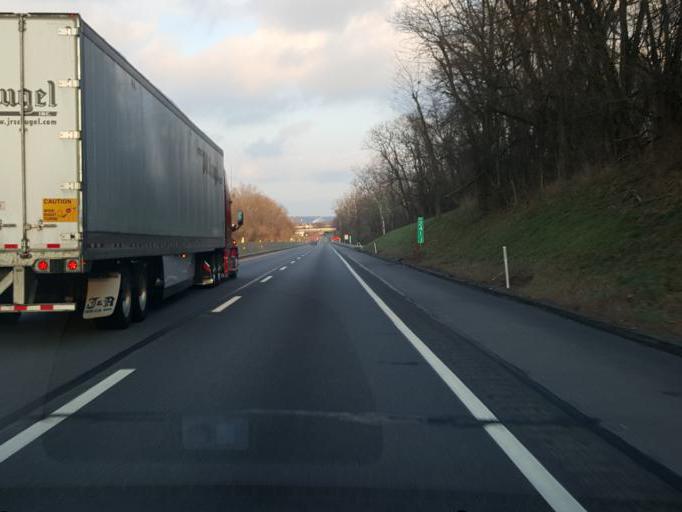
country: US
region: Pennsylvania
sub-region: Cumberland County
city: Lower Allen
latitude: 40.2072
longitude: -76.8903
